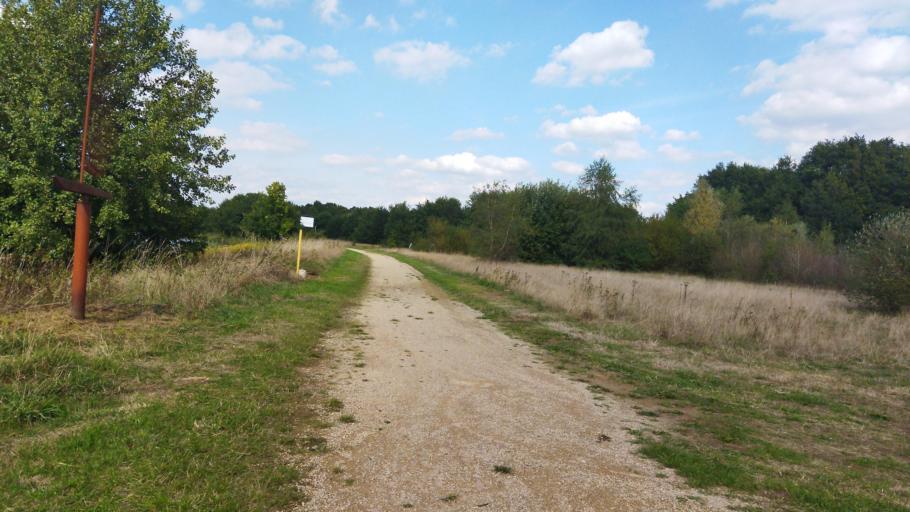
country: DE
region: Lower Saxony
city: Haren
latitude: 52.7785
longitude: 7.2608
